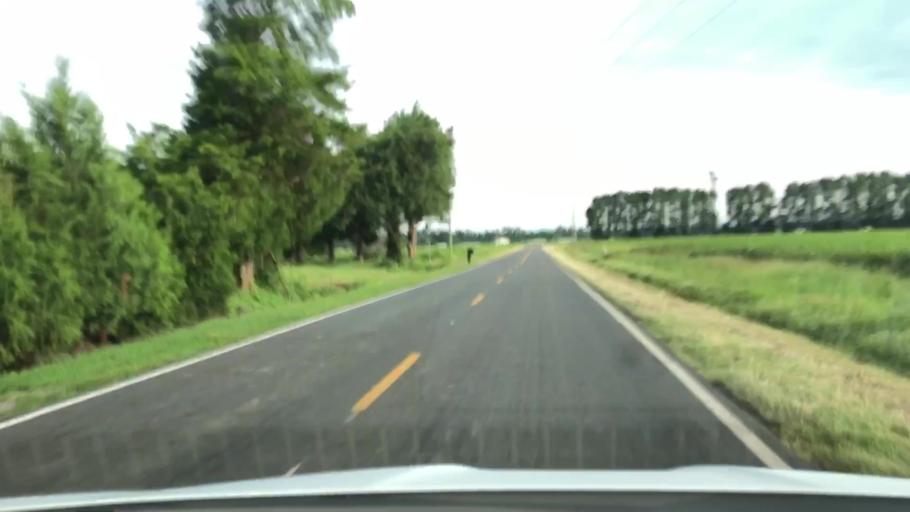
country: US
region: North Carolina
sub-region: Jones County
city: Maysville
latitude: 34.9876
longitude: -77.2791
